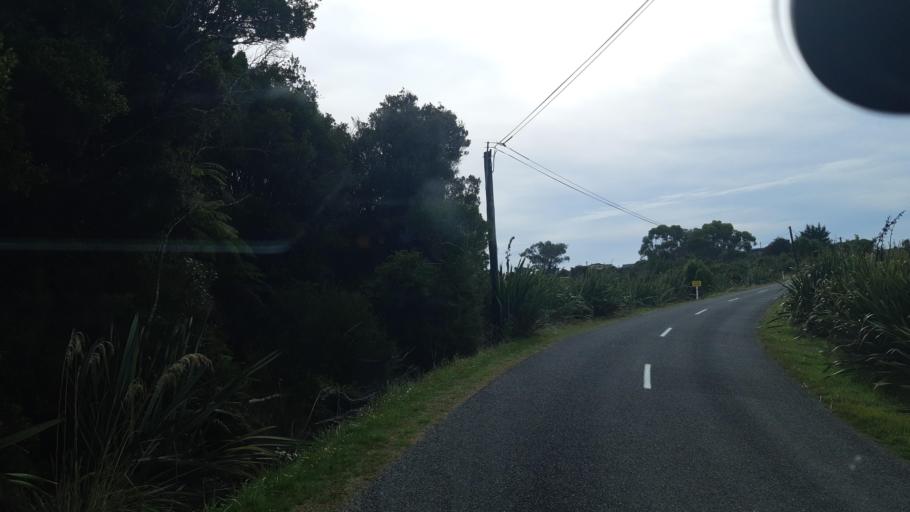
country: NZ
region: West Coast
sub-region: Westland District
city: Hokitika
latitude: -43.2231
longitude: 170.1695
